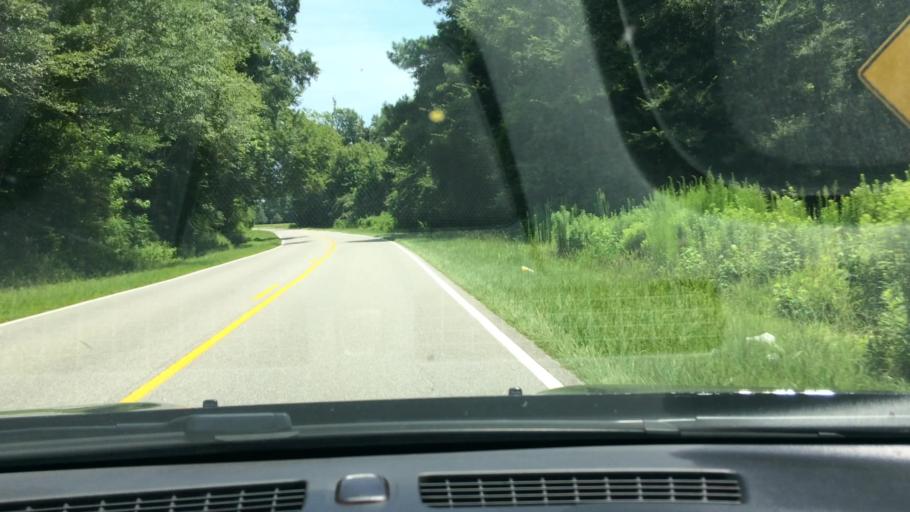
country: US
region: North Carolina
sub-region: Pitt County
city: Windsor
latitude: 35.5164
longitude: -77.3129
